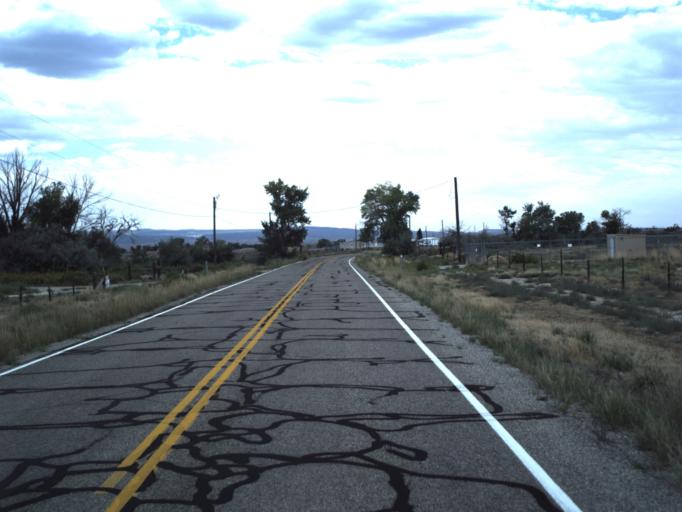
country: US
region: Utah
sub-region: Emery County
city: Huntington
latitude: 39.4098
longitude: -110.8536
